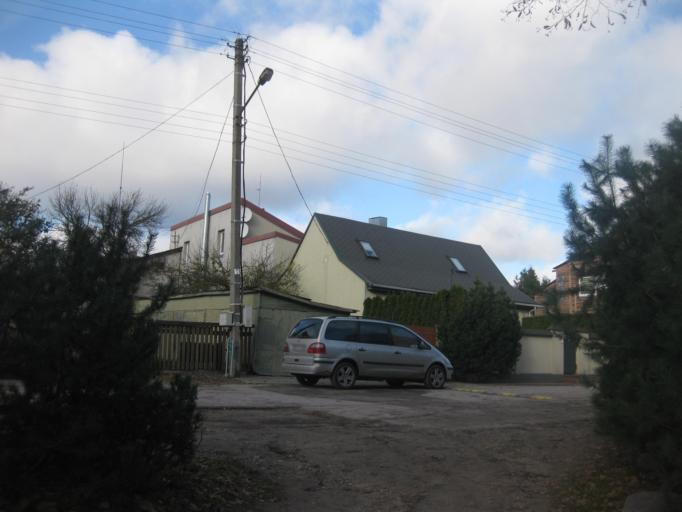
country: LT
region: Kauno apskritis
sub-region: Kaunas
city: Kaunas
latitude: 54.9081
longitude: 23.8926
